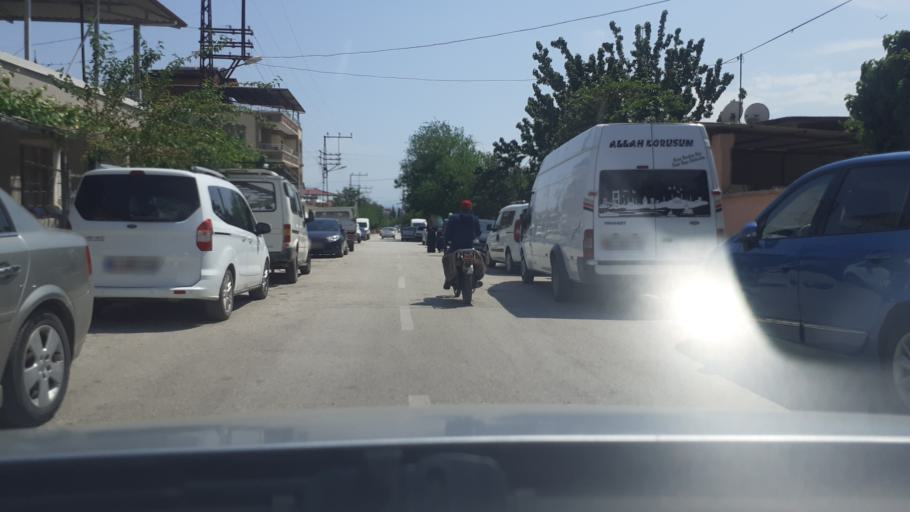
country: TR
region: Hatay
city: Kirikhan
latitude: 36.4922
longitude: 36.3540
